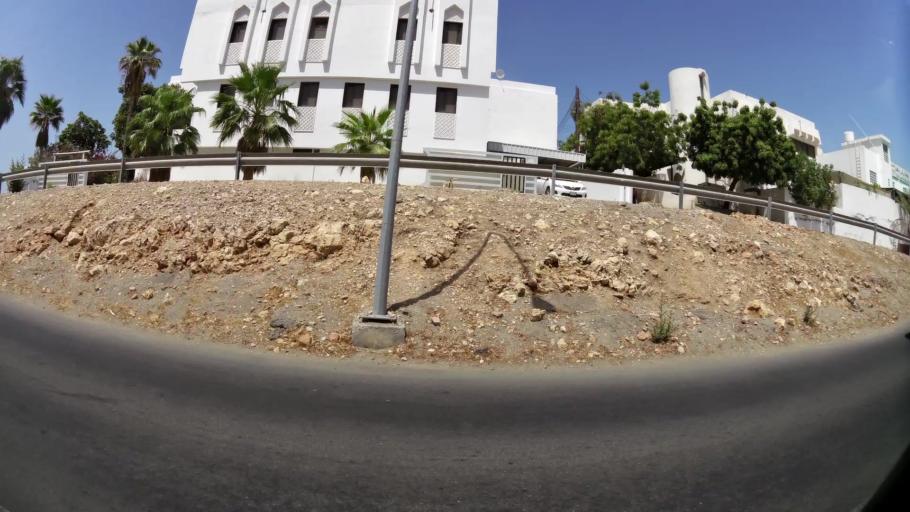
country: OM
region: Muhafazat Masqat
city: Muscat
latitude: 23.6175
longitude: 58.5037
